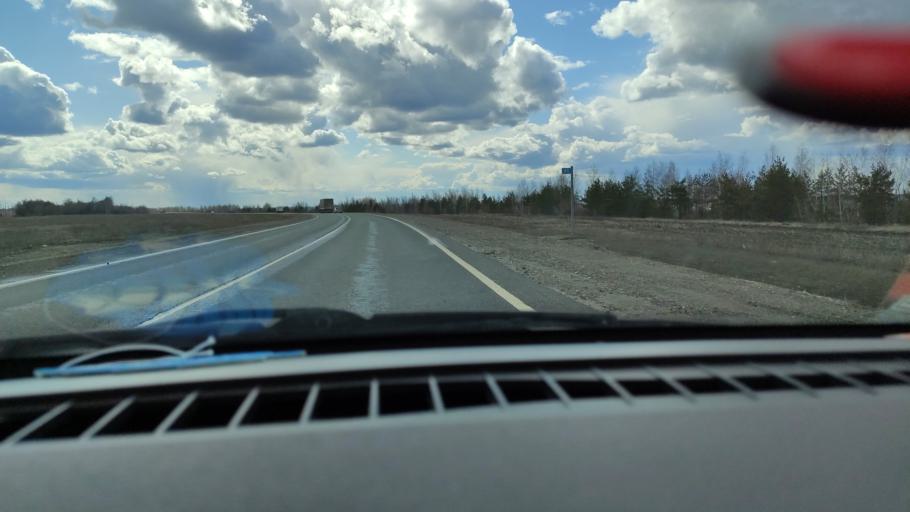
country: RU
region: Samara
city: Syzran'
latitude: 52.8615
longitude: 48.2650
